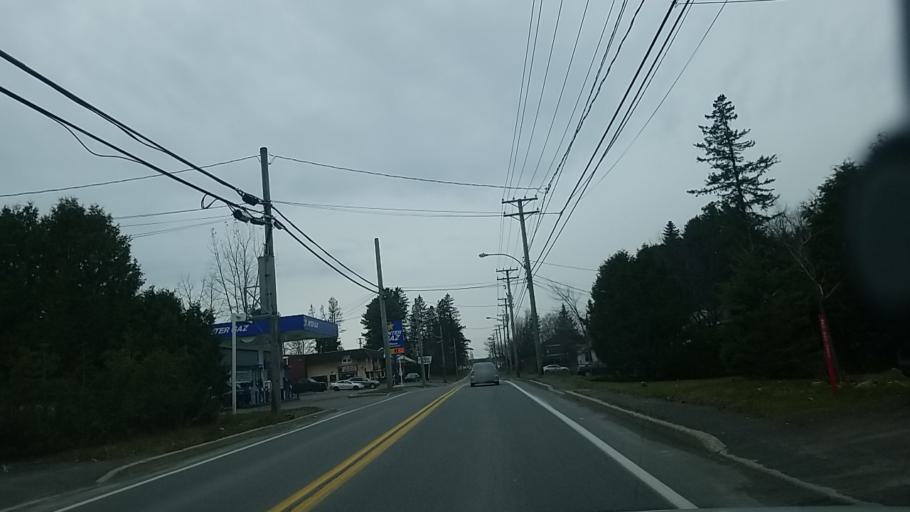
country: CA
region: Quebec
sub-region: Laurentides
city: Saint-Jerome
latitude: 45.7865
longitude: -74.0722
